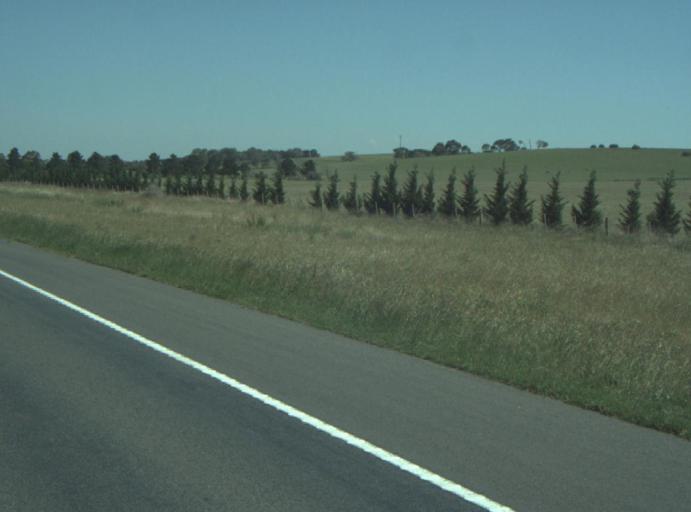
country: AU
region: Victoria
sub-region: Greater Geelong
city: Lara
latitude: -38.0185
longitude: 144.3522
